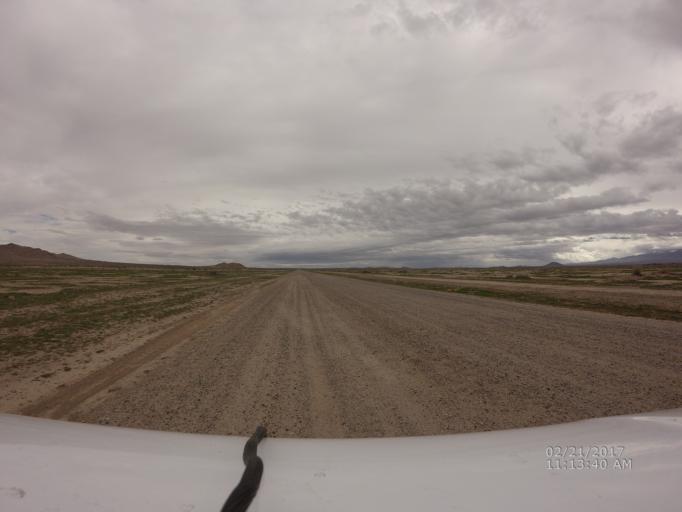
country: US
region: California
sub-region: Los Angeles County
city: Lake Los Angeles
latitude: 34.6459
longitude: -117.8207
